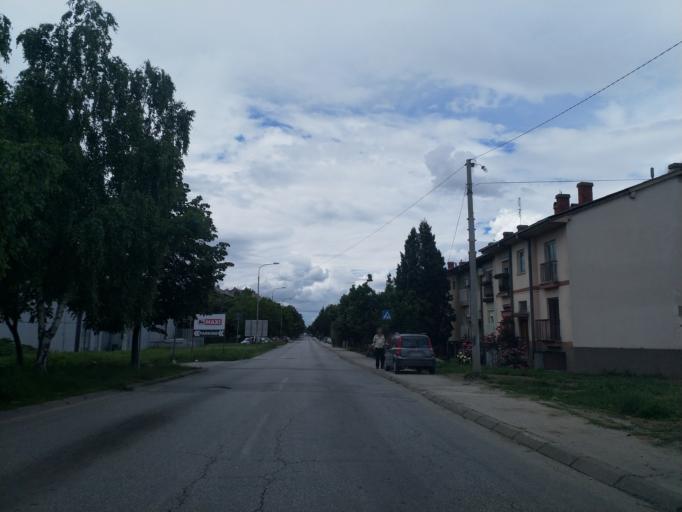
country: RS
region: Central Serbia
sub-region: Pomoravski Okrug
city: Jagodina
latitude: 43.9661
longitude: 21.2772
